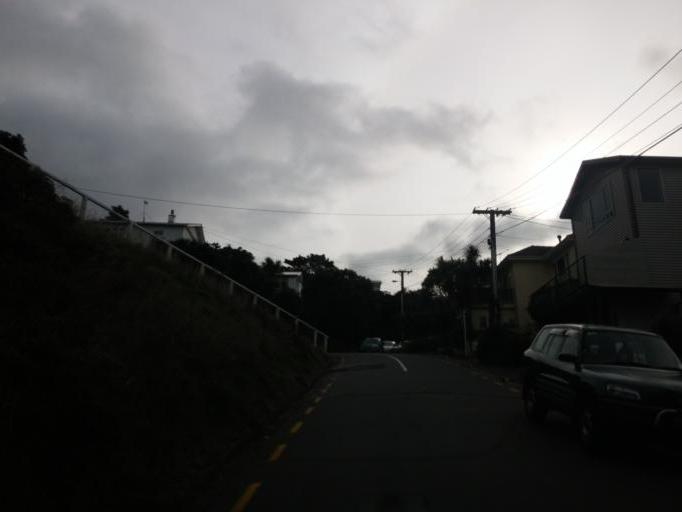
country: NZ
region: Wellington
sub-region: Wellington City
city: Brooklyn
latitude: -41.3123
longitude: 174.7666
